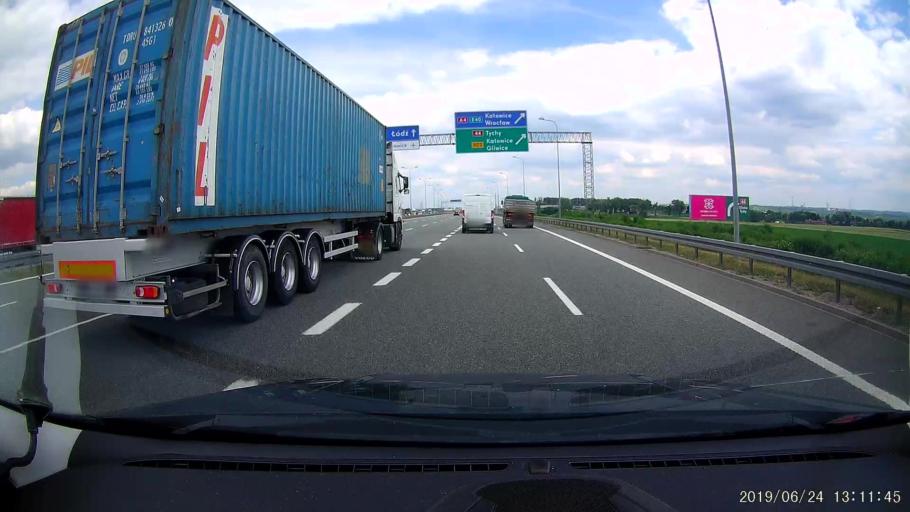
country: PL
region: Silesian Voivodeship
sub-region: Powiat gliwicki
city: Gieraltowice
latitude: 50.2487
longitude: 18.7151
